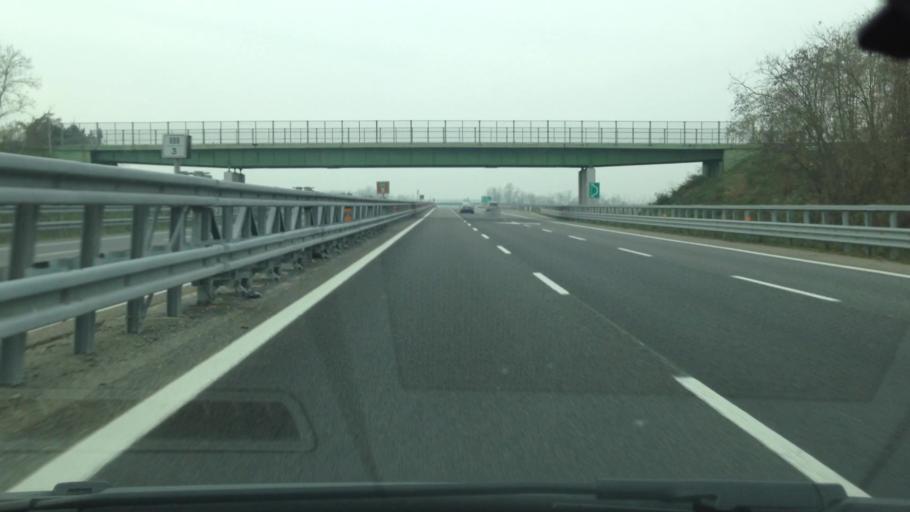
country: IT
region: Piedmont
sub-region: Provincia di Torino
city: Pessione
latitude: 44.9578
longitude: 7.8283
